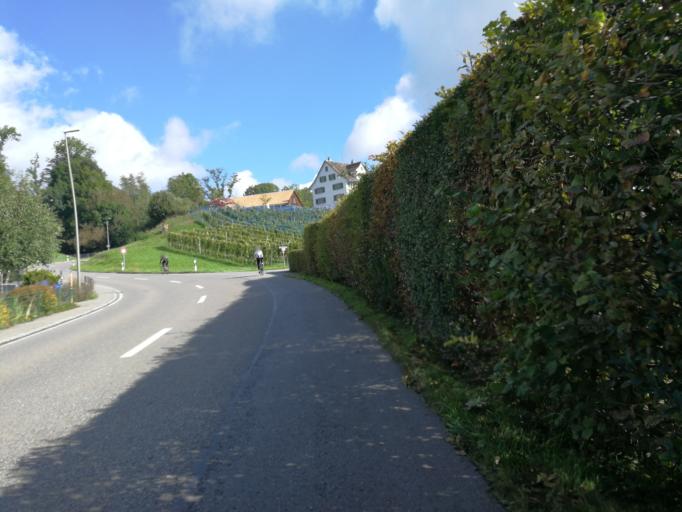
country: CH
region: Zurich
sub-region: Bezirk Meilen
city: Uerikon
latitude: 47.2414
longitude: 8.7598
